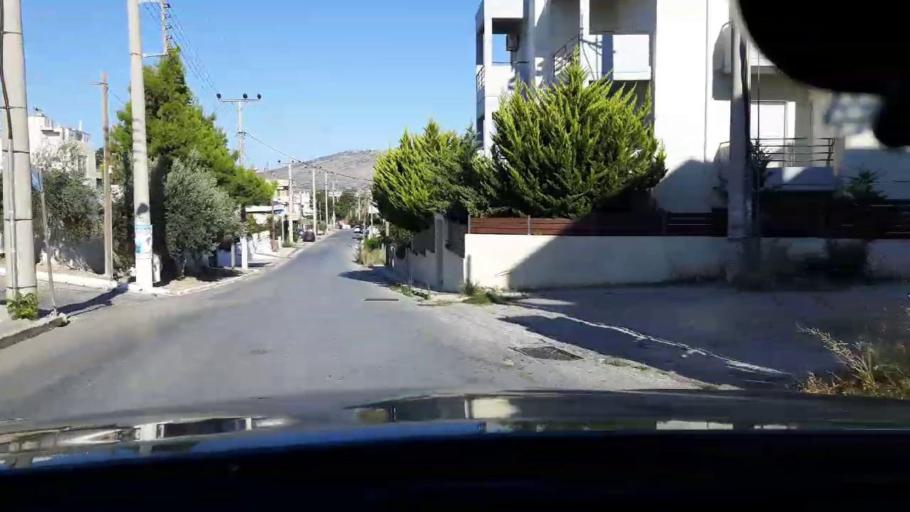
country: GR
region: Attica
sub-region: Nomarchia Anatolikis Attikis
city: Markopoulo
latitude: 37.8828
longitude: 23.9395
